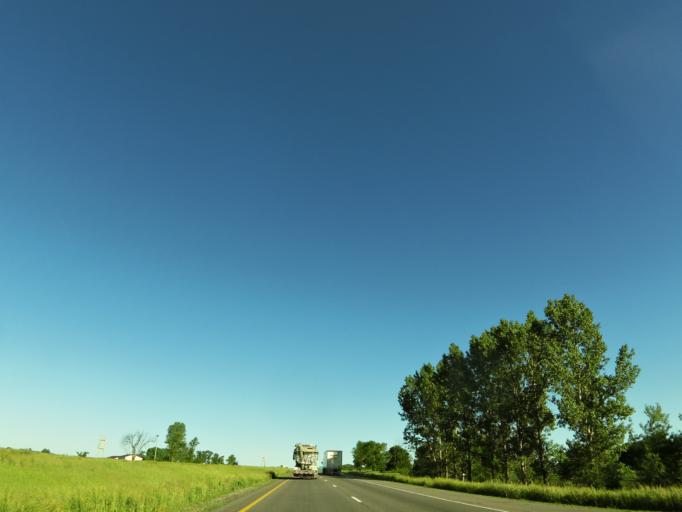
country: US
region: Minnesota
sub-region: Stearns County
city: Melrose
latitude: 45.6904
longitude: -94.8678
